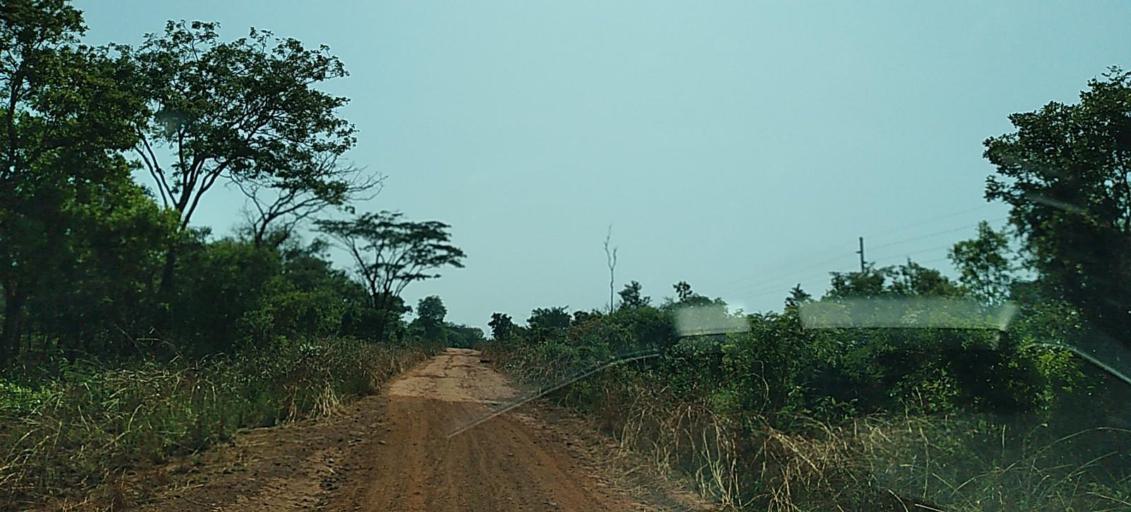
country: ZM
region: North-Western
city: Kansanshi
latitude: -12.0098
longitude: 26.5103
